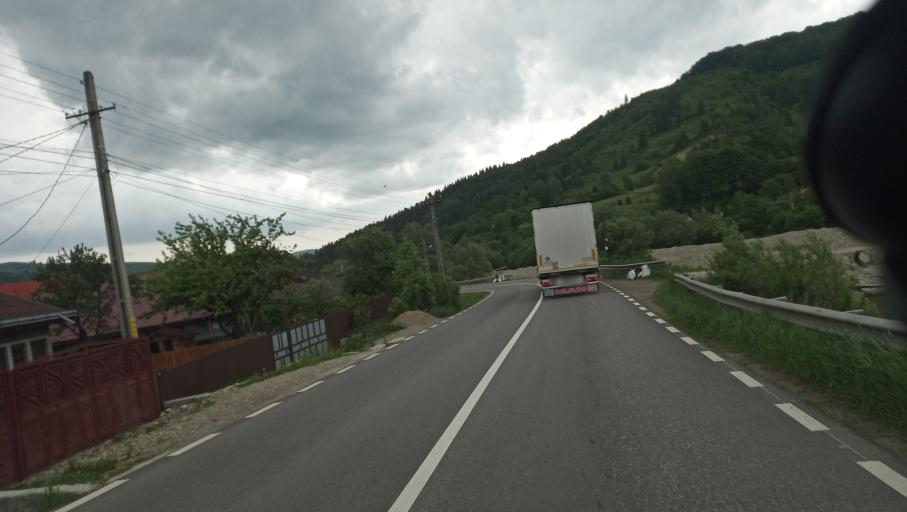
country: RO
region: Neamt
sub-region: Comuna Pipirig
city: Dolhesti
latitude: 47.2245
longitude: 26.0744
